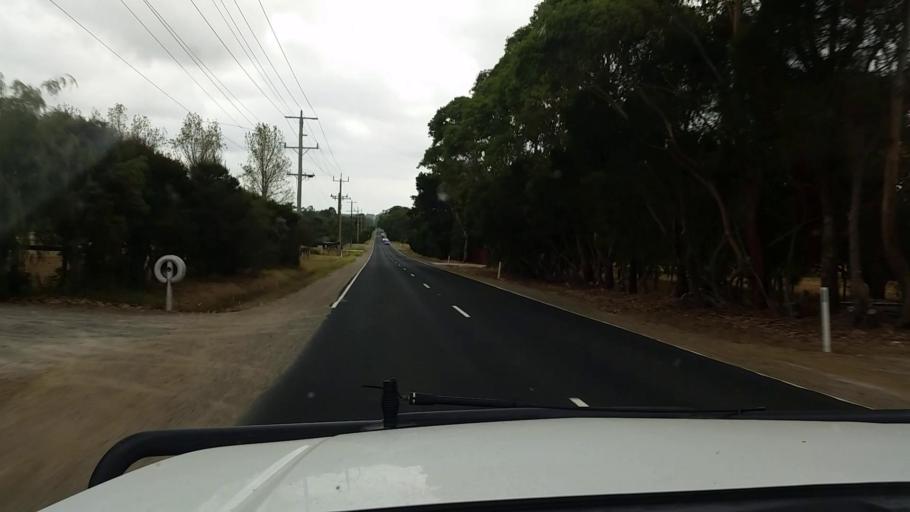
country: AU
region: Victoria
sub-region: Mornington Peninsula
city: Somerville
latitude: -38.2171
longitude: 145.1557
